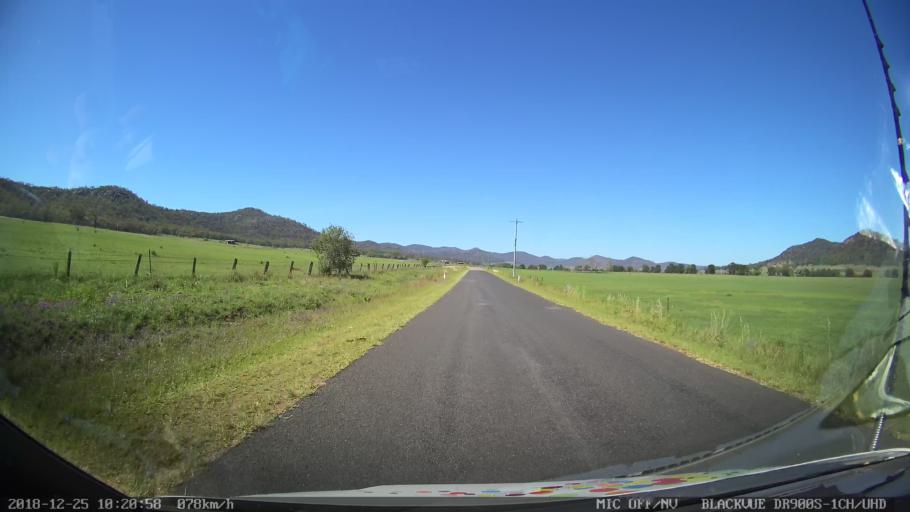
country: AU
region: New South Wales
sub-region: Muswellbrook
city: Denman
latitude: -32.3626
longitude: 150.5444
